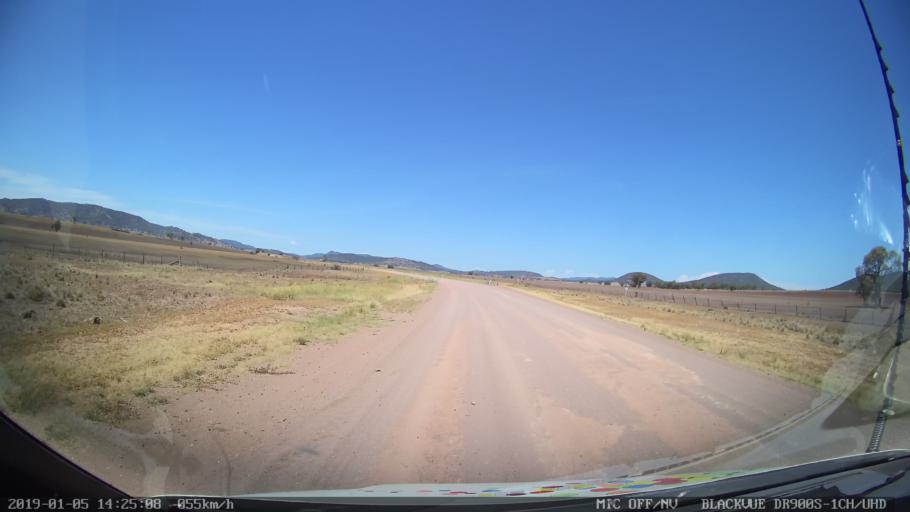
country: AU
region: New South Wales
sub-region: Liverpool Plains
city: Quirindi
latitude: -31.2415
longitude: 150.5470
